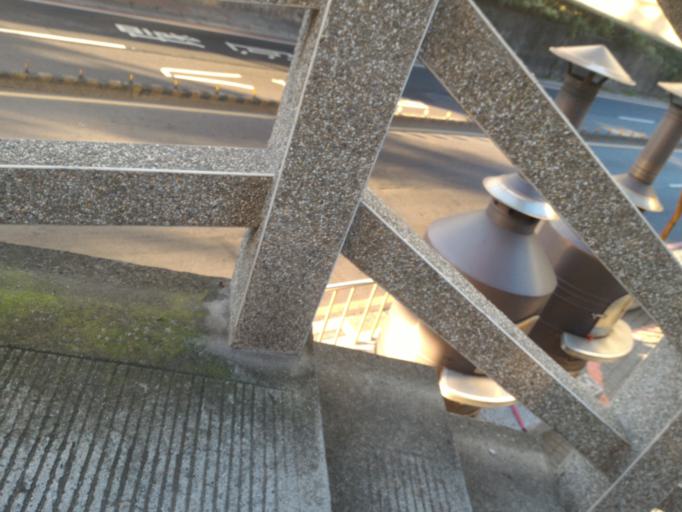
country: TW
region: Taiwan
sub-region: Taoyuan
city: Taoyuan
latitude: 24.9687
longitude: 121.3938
